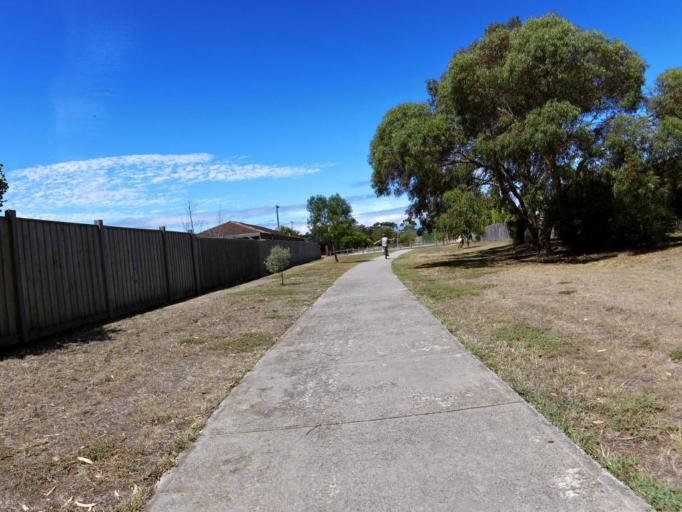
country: AU
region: Victoria
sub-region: Hobsons Bay
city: Altona Meadows
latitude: -37.8814
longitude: 144.7902
